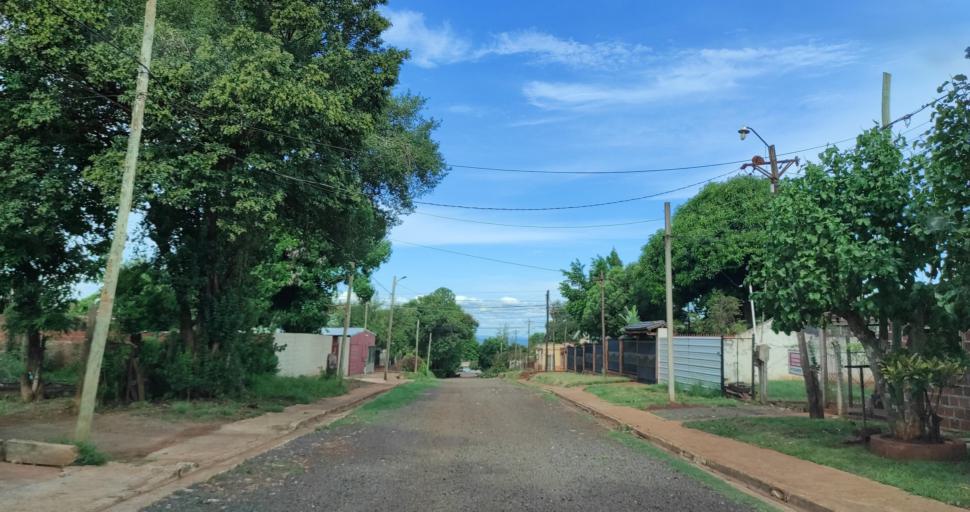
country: AR
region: Misiones
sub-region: Departamento de Capital
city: Posadas
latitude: -27.4068
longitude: -55.9141
